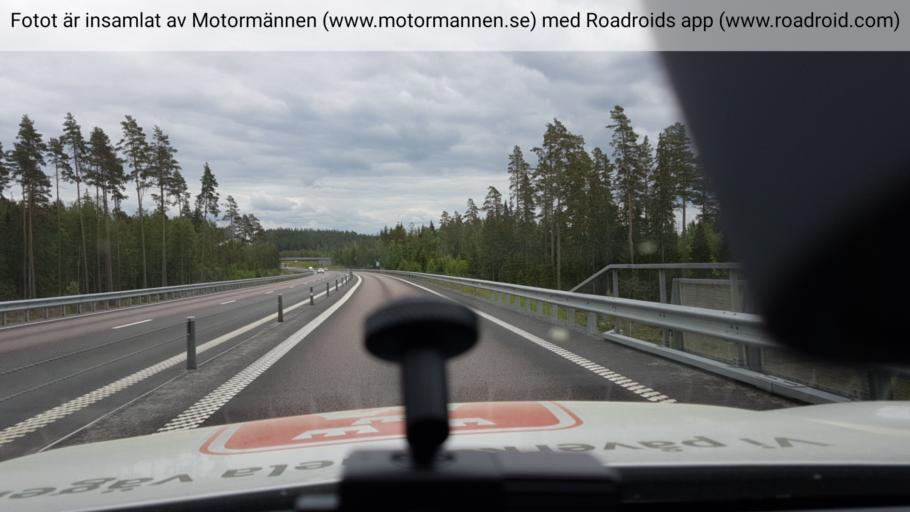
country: SE
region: Joenkoeping
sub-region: Mullsjo Kommun
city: Mullsjoe
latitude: 57.8907
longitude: 13.8889
